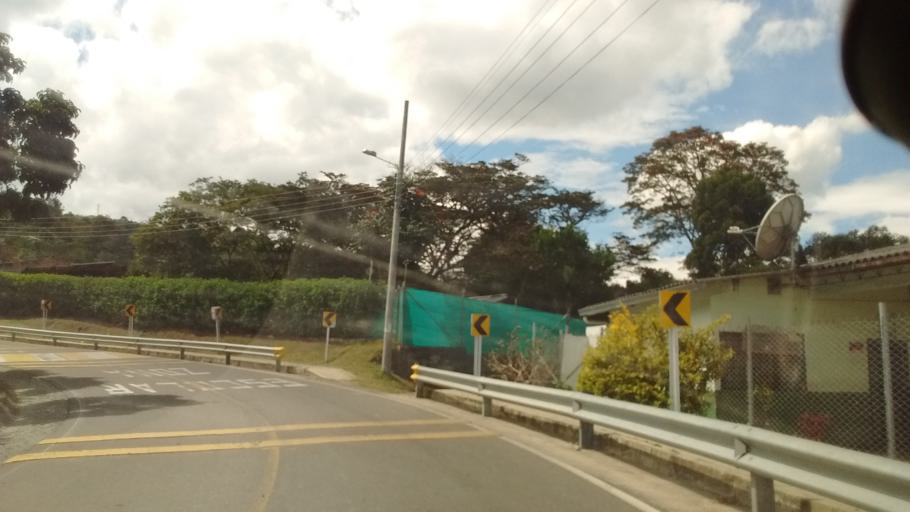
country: CO
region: Cauca
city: Cajibio
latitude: 2.6270
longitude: -76.5160
